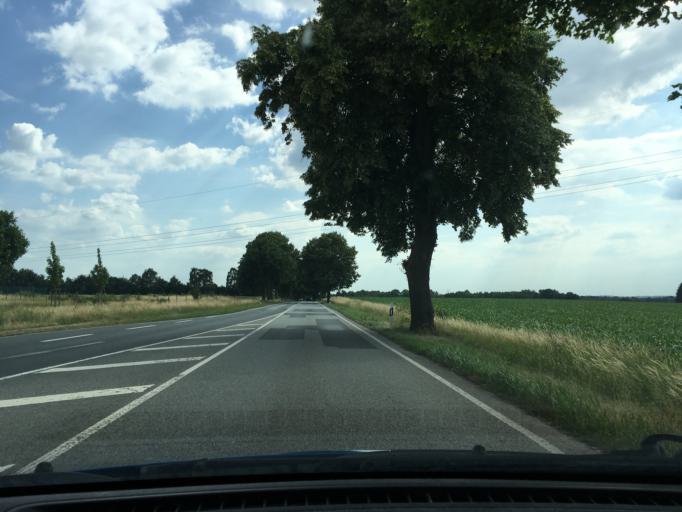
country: DE
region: Lower Saxony
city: Kakenstorf
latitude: 53.3214
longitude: 9.8092
